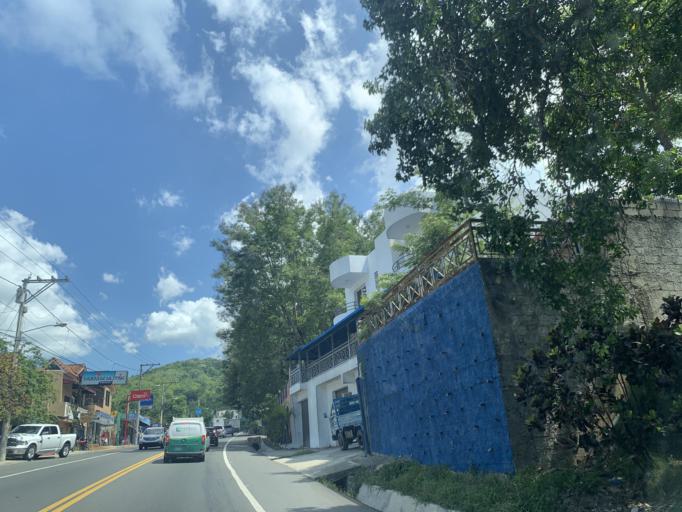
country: DO
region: Puerto Plata
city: Altamira
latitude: 19.6758
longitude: -70.8355
